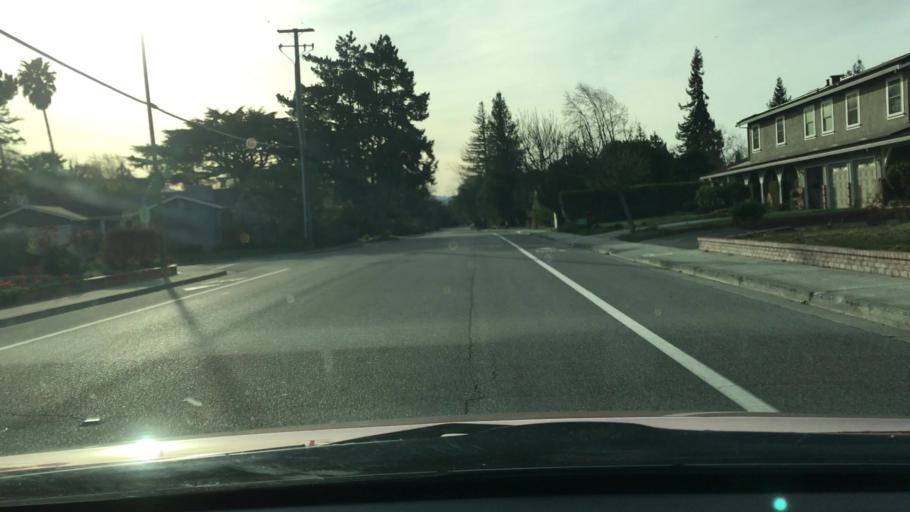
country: US
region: California
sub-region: Santa Clara County
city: Mountain View
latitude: 37.3613
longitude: -122.0733
